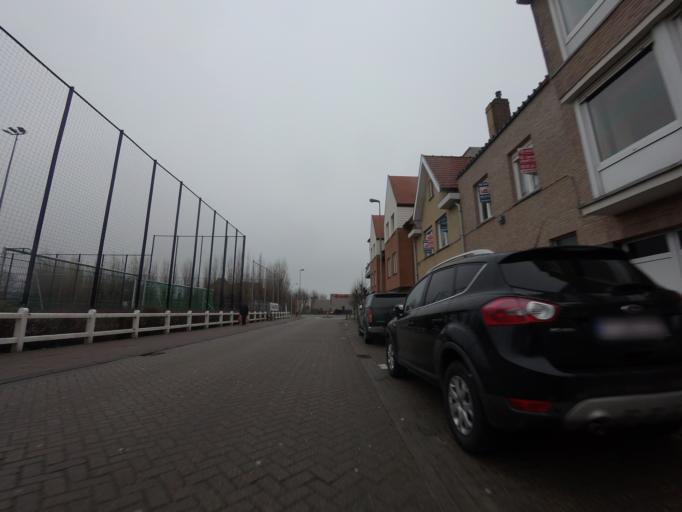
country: BE
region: Flanders
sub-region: Provincie West-Vlaanderen
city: Knokke-Heist
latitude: 51.3381
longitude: 3.2901
